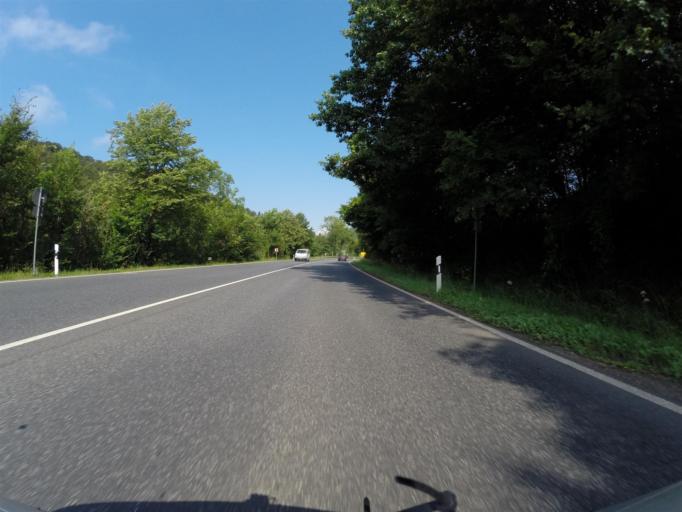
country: DE
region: Hesse
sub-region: Regierungsbezirk Kassel
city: Grossalmerode
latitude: 51.1797
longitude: 9.8031
